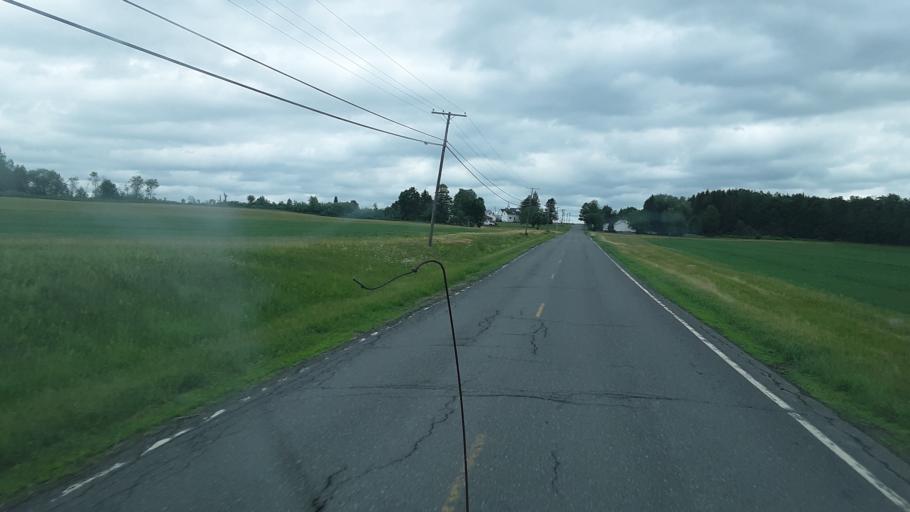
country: US
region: Maine
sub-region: Aroostook County
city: Caribou
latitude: 46.8270
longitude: -68.1744
